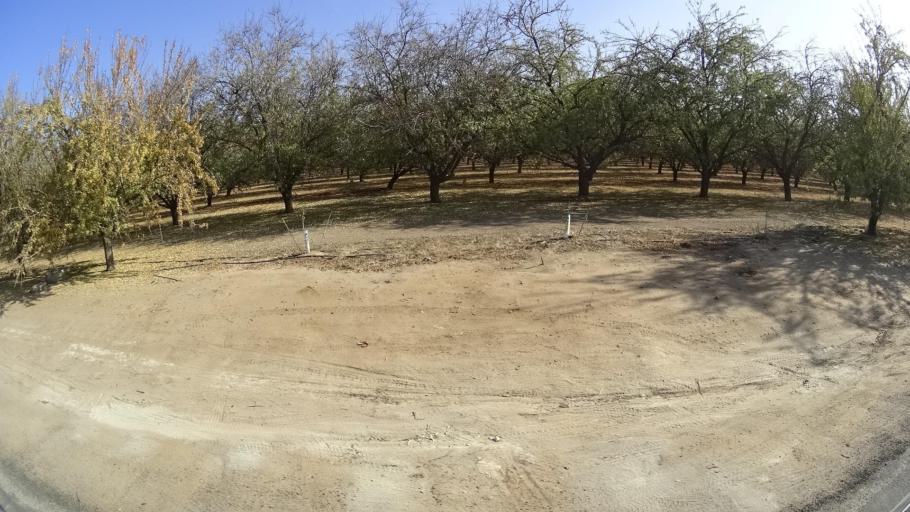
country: US
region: California
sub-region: Kern County
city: McFarland
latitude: 35.6386
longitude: -119.1867
